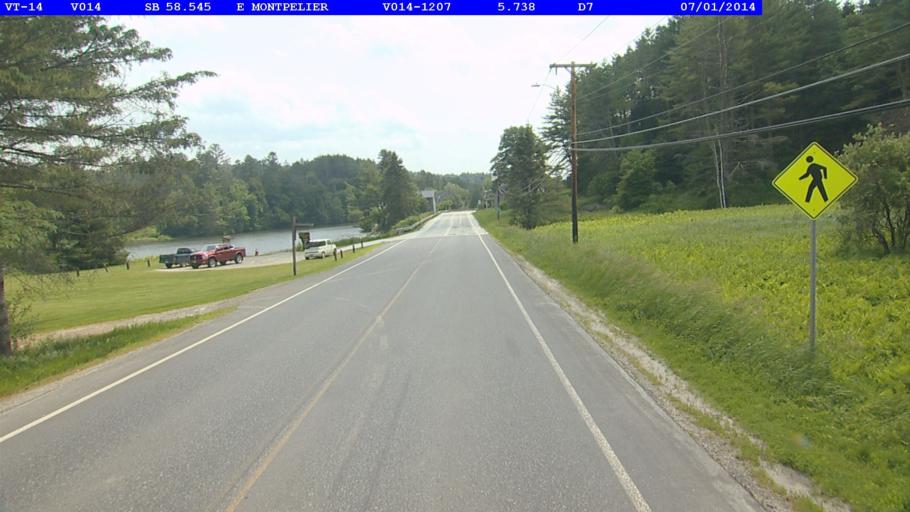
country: US
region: Vermont
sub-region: Washington County
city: Barre
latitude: 44.3066
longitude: -72.4470
